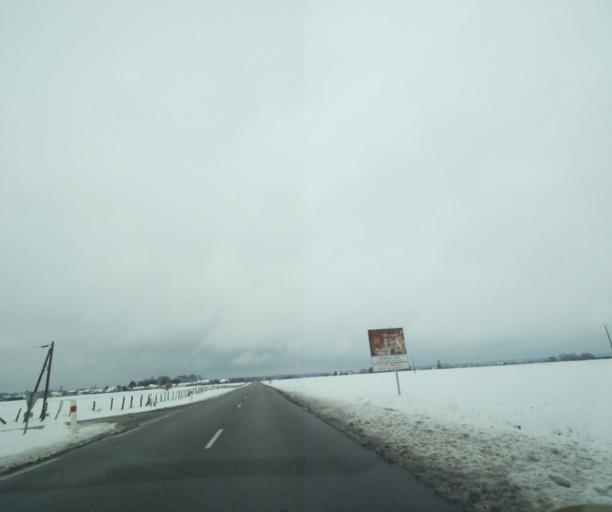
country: FR
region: Champagne-Ardenne
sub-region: Departement de la Haute-Marne
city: Montier-en-Der
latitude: 48.4614
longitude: 4.7573
